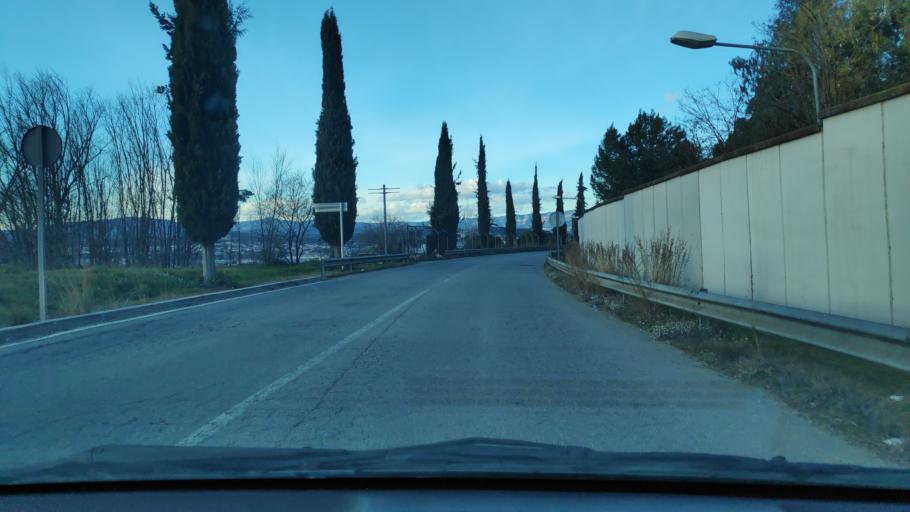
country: ES
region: Catalonia
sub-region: Provincia de Barcelona
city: Montmelo
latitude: 41.5647
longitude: 2.2514
